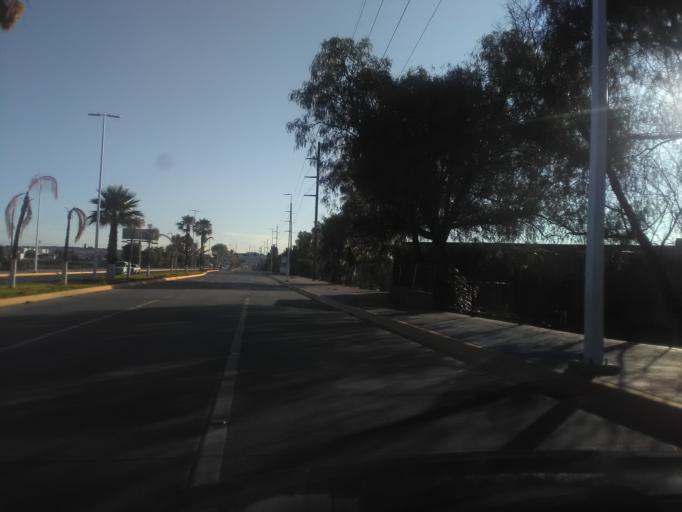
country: MX
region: Durango
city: Victoria de Durango
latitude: 23.9937
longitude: -104.7046
